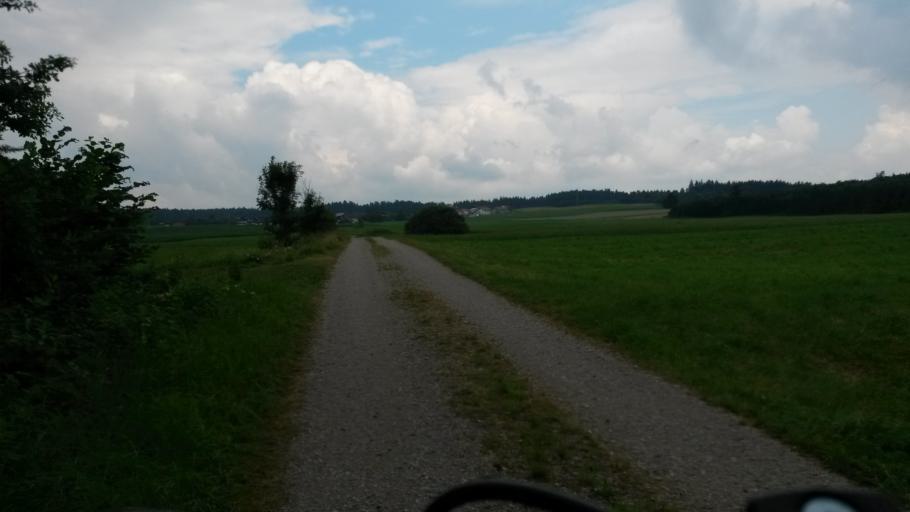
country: DE
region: Bavaria
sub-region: Upper Bavaria
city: Hoslwang
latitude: 47.9386
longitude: 12.3272
